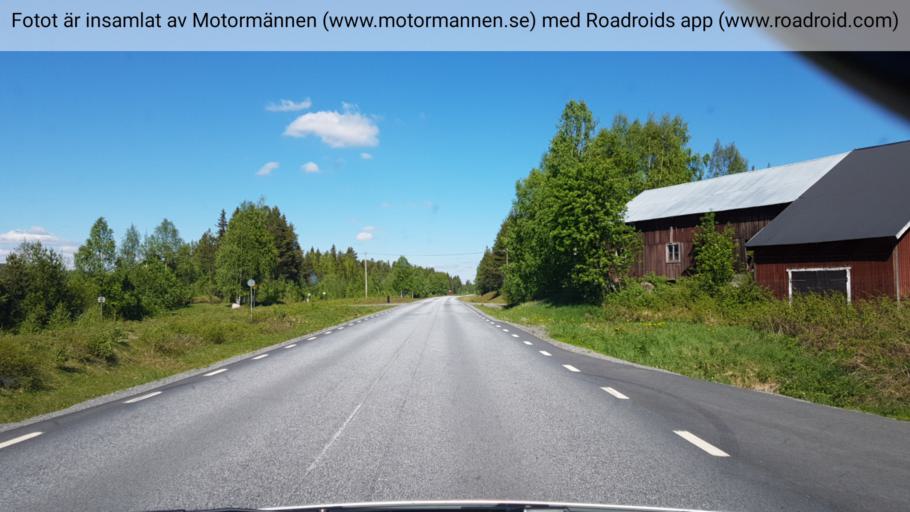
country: SE
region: Vaesterbotten
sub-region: Vilhelmina Kommun
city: Vilhelmina
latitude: 64.4705
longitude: 16.7975
